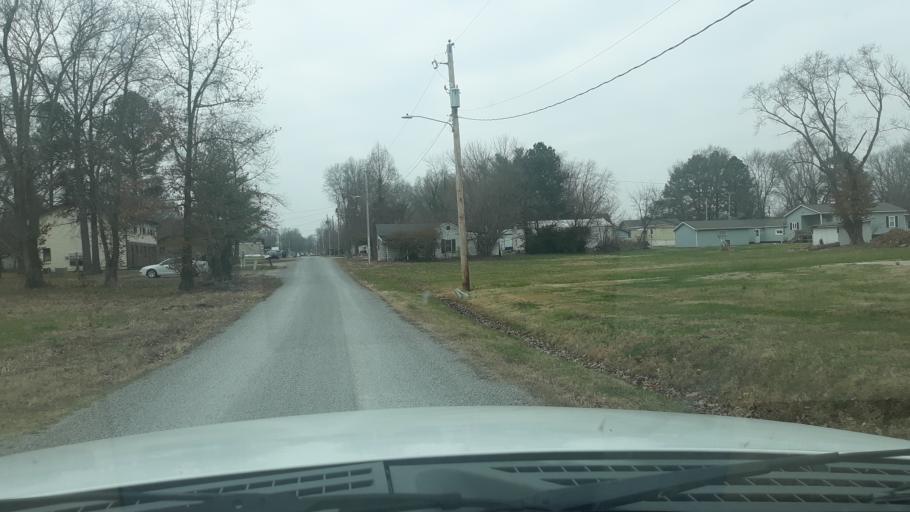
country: US
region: Illinois
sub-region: Saline County
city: Harrisburg
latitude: 37.8391
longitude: -88.6030
